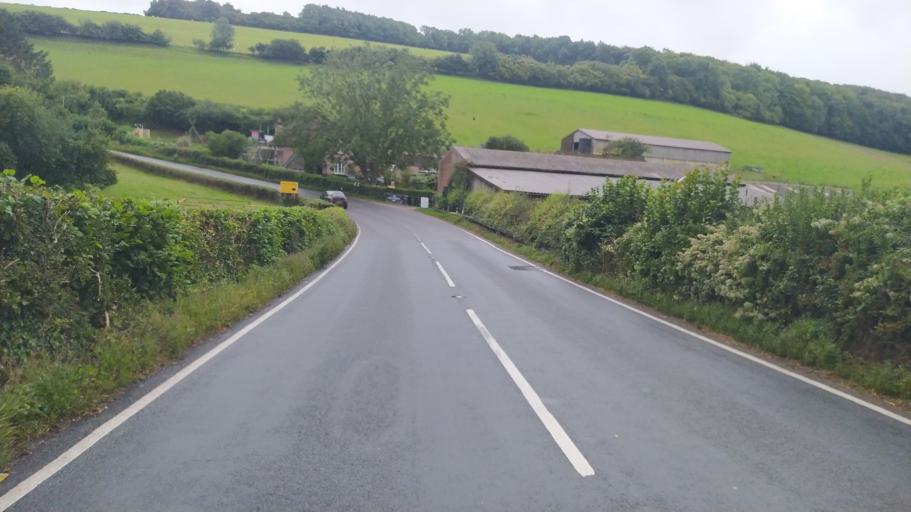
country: GB
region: England
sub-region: Dorset
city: Blandford Forum
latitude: 50.8845
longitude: -2.2167
